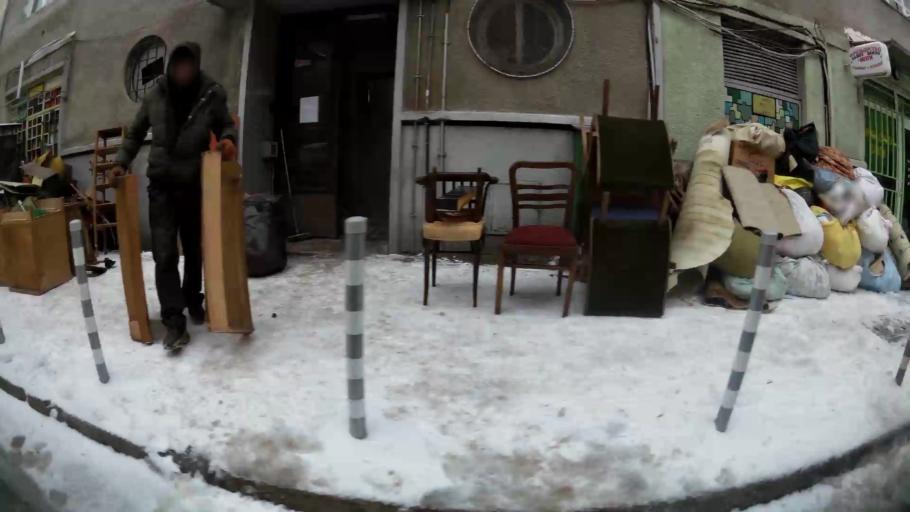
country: BG
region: Sofia-Capital
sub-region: Stolichna Obshtina
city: Sofia
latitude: 42.6913
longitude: 23.3420
